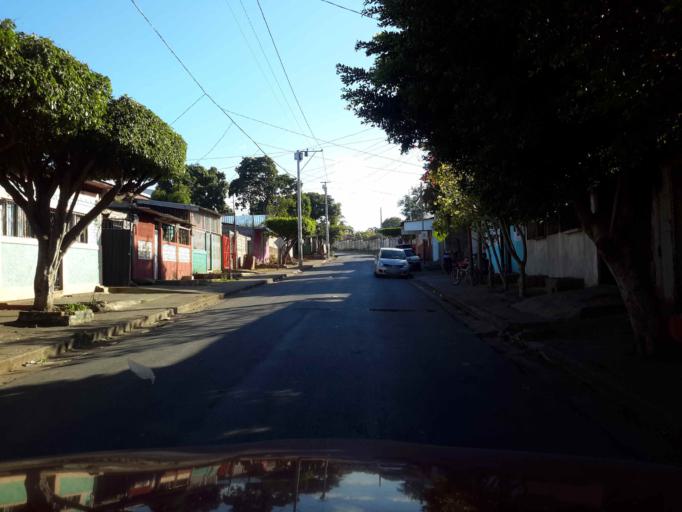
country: NI
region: Managua
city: Managua
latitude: 12.1166
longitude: -86.2940
